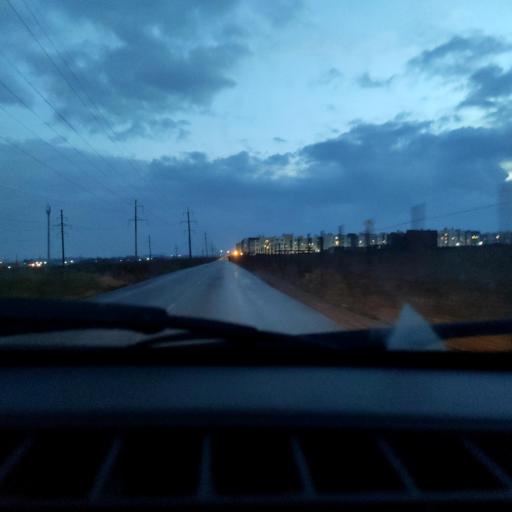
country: RU
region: Bashkortostan
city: Mikhaylovka
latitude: 54.7486
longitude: 55.7943
